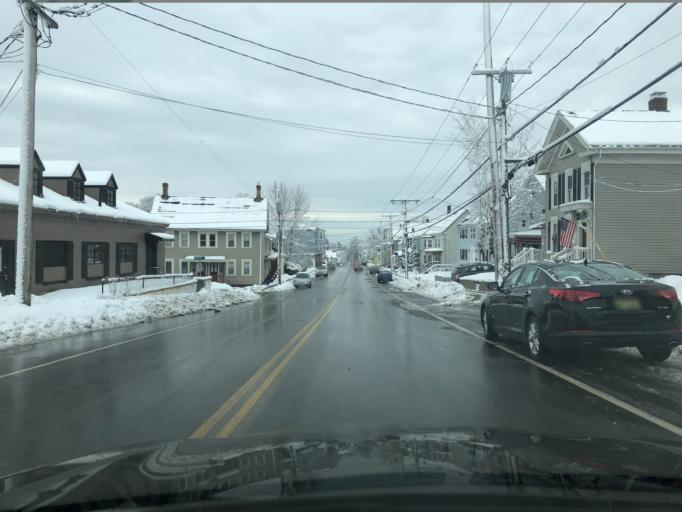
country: US
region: New Hampshire
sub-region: Strafford County
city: Somersworth
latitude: 43.2590
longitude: -70.8641
